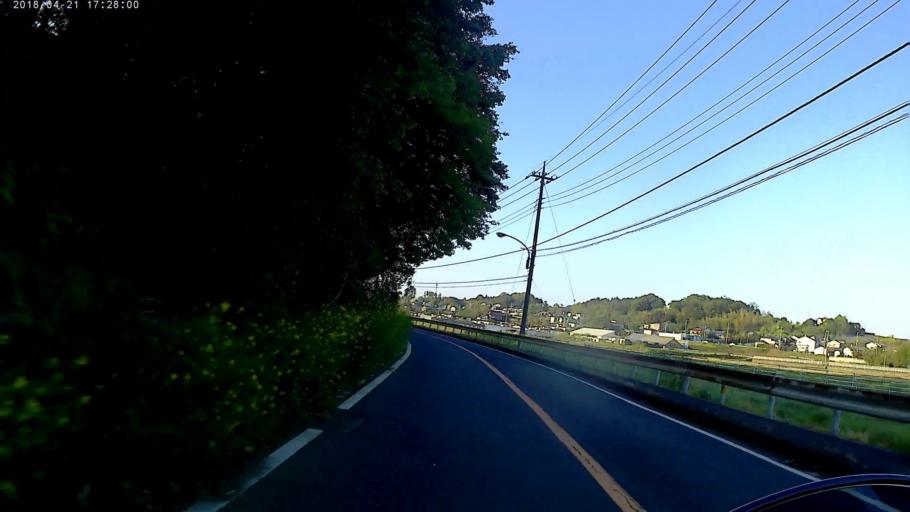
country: JP
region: Kanagawa
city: Atsugi
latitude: 35.4199
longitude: 139.4129
